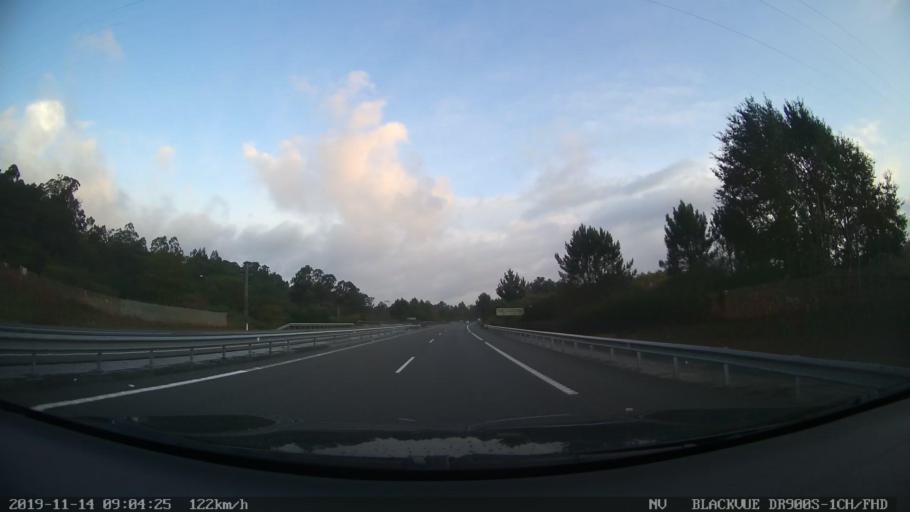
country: ES
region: Galicia
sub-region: Provincia de Pontevedra
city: Tui
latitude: 42.0948
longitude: -8.6436
